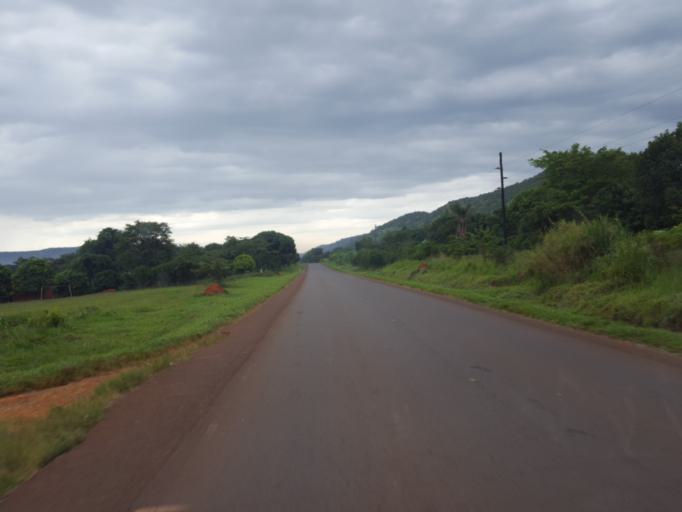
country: UG
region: Central Region
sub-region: Kiboga District
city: Kiboga
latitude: 0.8473
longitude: 31.8753
